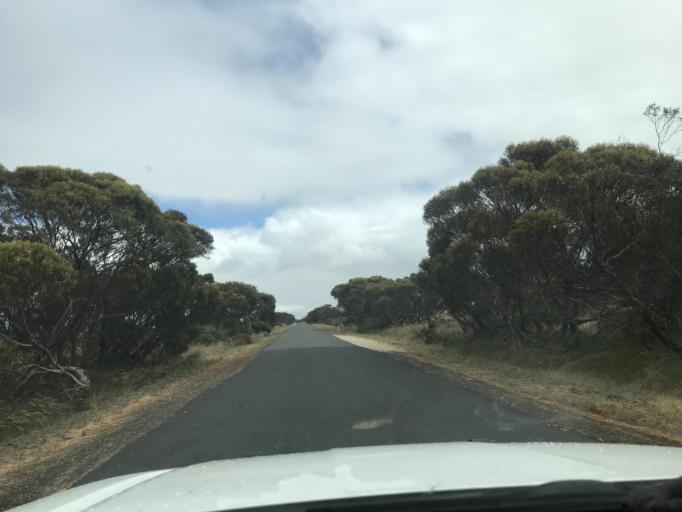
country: AU
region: South Australia
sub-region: Tatiara
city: Bordertown
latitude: -36.1451
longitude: 141.2321
